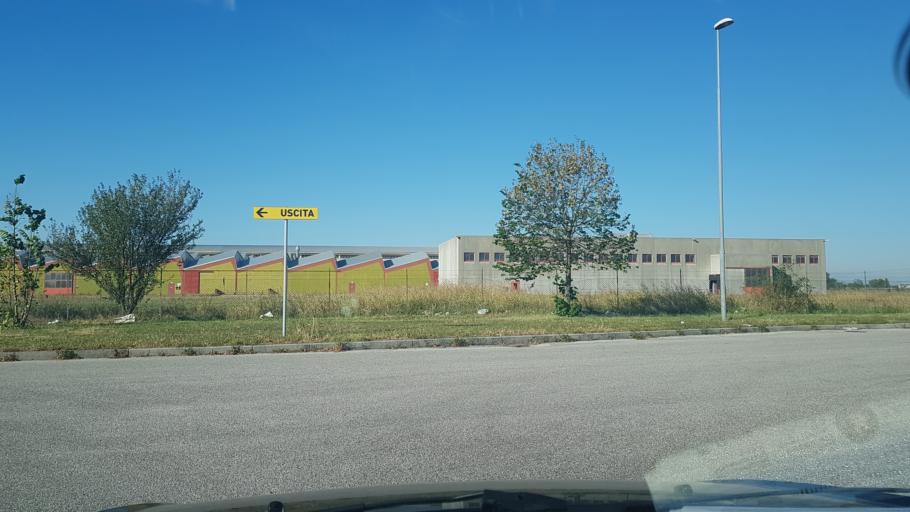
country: IT
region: Friuli Venezia Giulia
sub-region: Provincia di Gorizia
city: Mariano del Friuli
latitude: 45.8954
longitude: 13.4718
